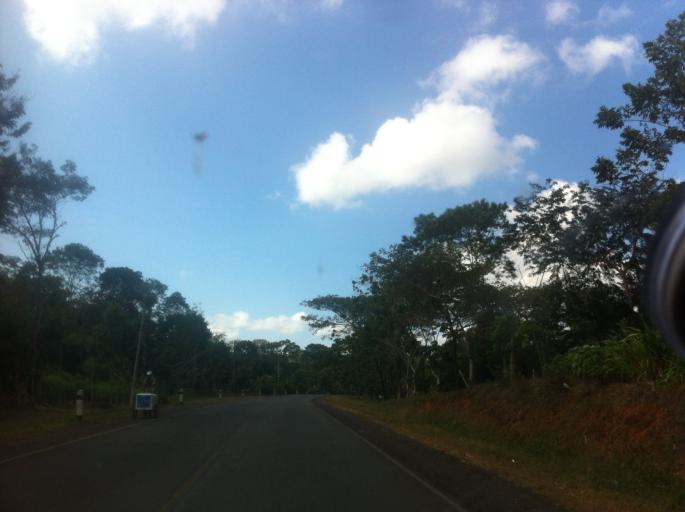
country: NI
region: Rio San Juan
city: San Carlos
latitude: 11.2043
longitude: -84.7305
